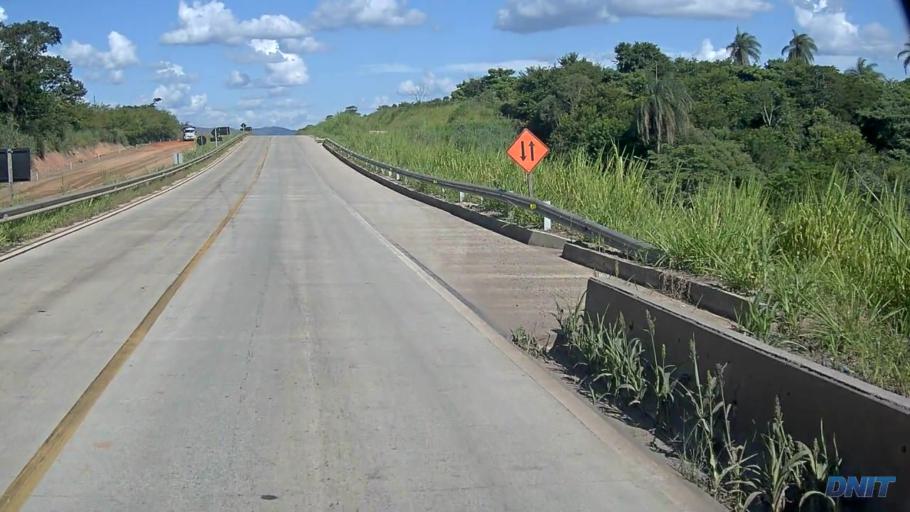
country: BR
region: Minas Gerais
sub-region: Barao De Cocais
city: Barao de Cocais
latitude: -19.7739
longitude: -43.4451
